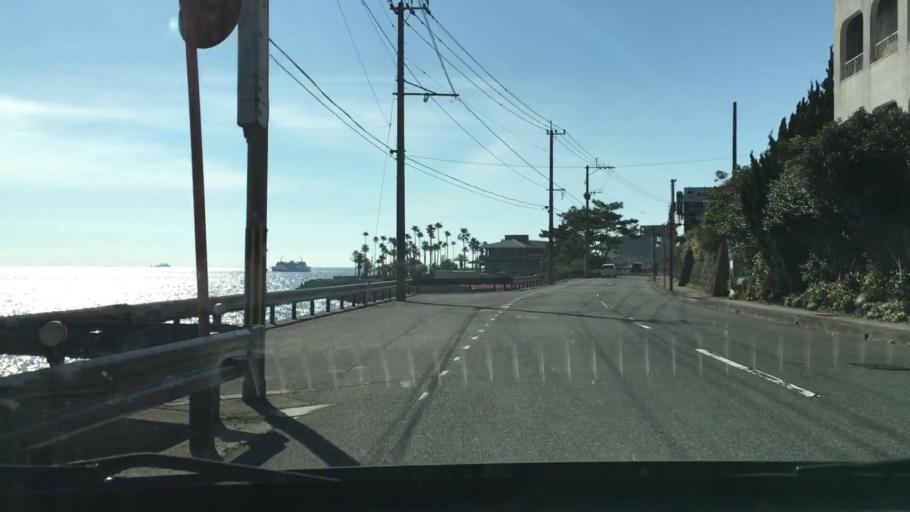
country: JP
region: Kagoshima
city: Kagoshima-shi
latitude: 31.6097
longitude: 130.5746
